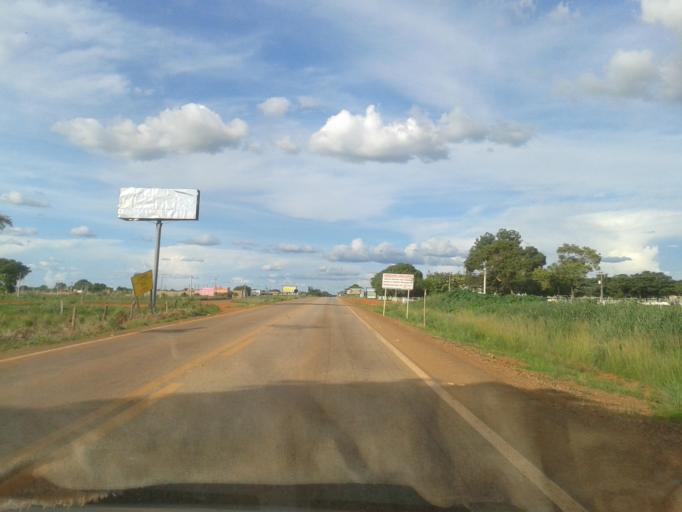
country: BR
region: Goias
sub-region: Crixas
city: Crixas
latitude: -14.1174
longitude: -50.3453
